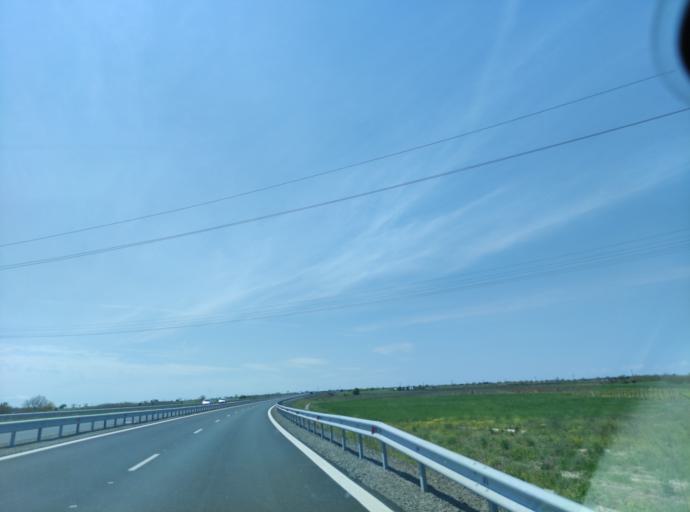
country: BG
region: Burgas
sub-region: Obshtina Pomorie
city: Pomorie
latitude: 42.5914
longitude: 27.6102
